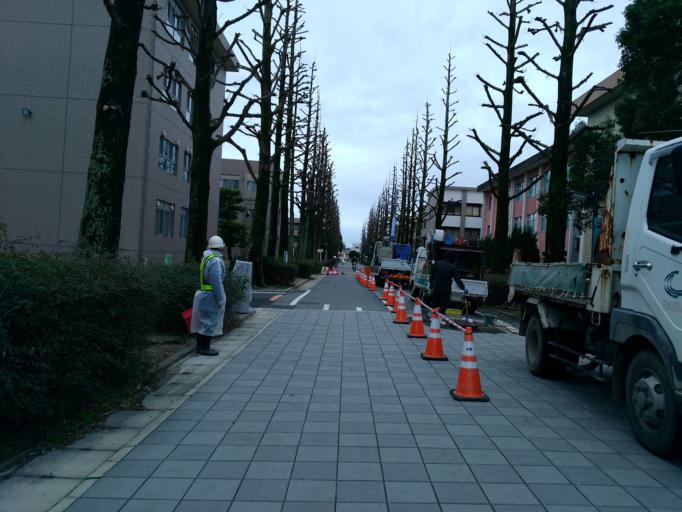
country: JP
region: Saga Prefecture
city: Saga-shi
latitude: 33.2442
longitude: 130.2925
